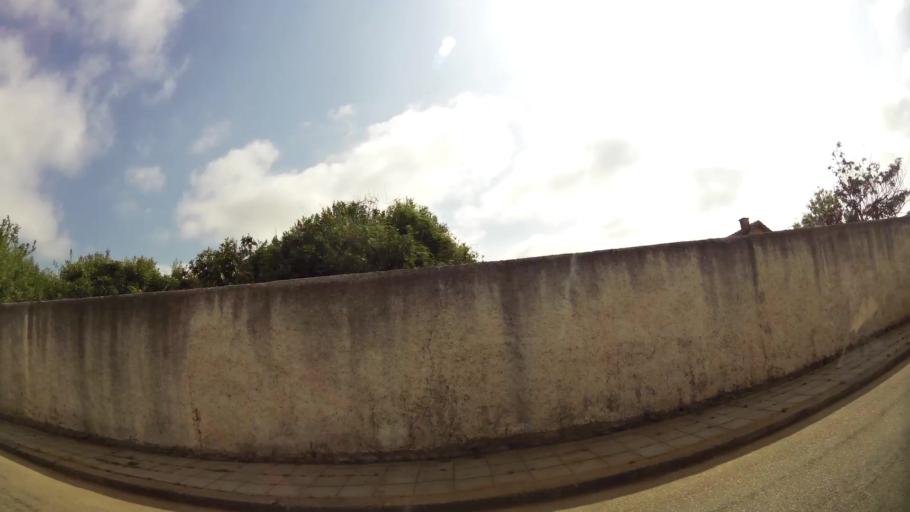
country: MA
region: Rabat-Sale-Zemmour-Zaer
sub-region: Rabat
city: Rabat
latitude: 33.9720
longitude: -6.8451
